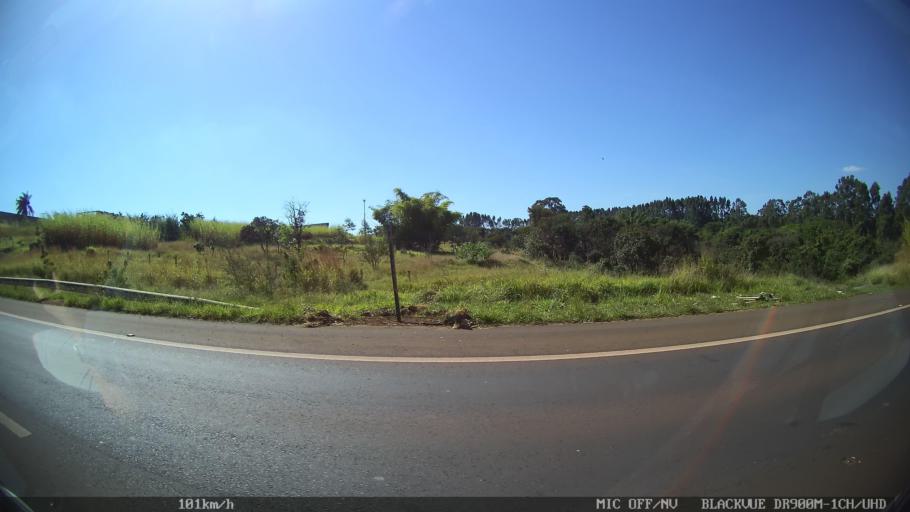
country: BR
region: Sao Paulo
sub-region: Franca
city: Franca
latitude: -20.5509
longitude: -47.4534
